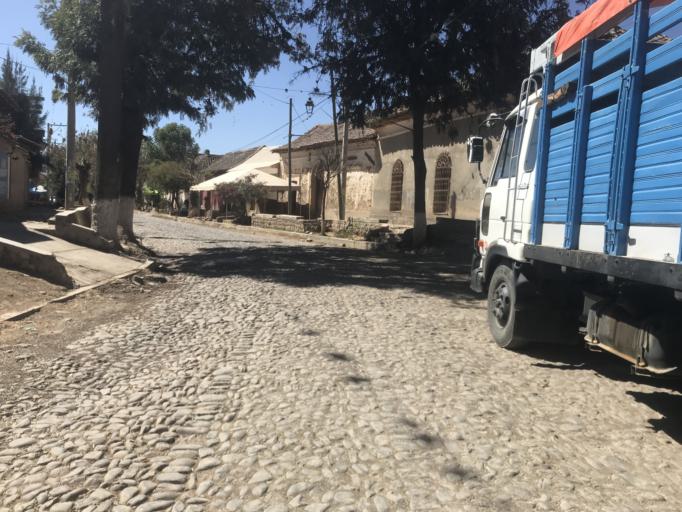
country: BO
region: Cochabamba
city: Tarata
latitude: -17.6139
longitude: -66.0251
